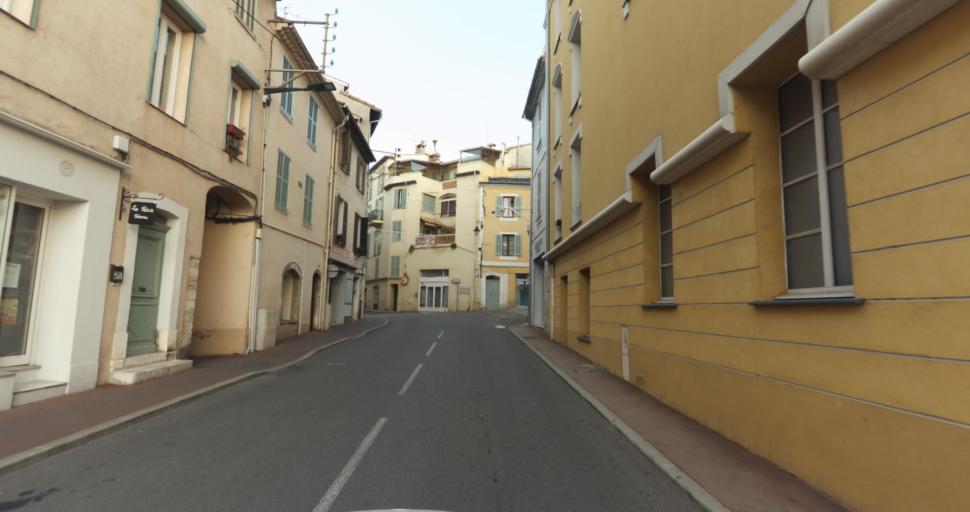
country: FR
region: Provence-Alpes-Cote d'Azur
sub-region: Departement des Alpes-Maritimes
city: Vence
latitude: 43.7214
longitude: 7.1150
